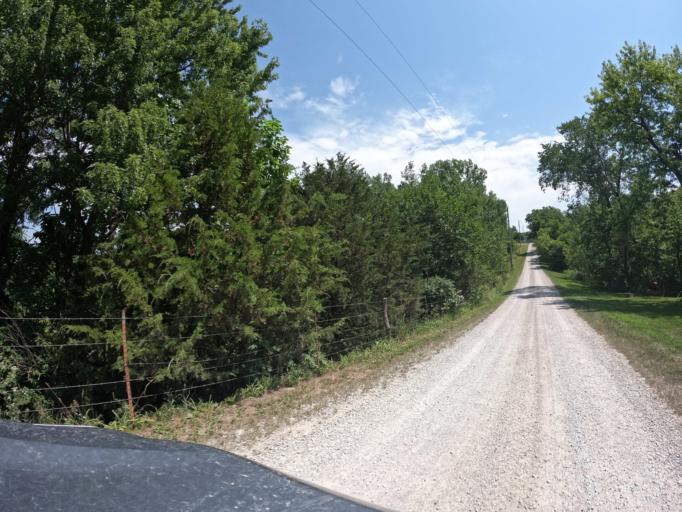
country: US
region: Iowa
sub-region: Appanoose County
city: Centerville
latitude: 40.7825
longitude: -92.9481
